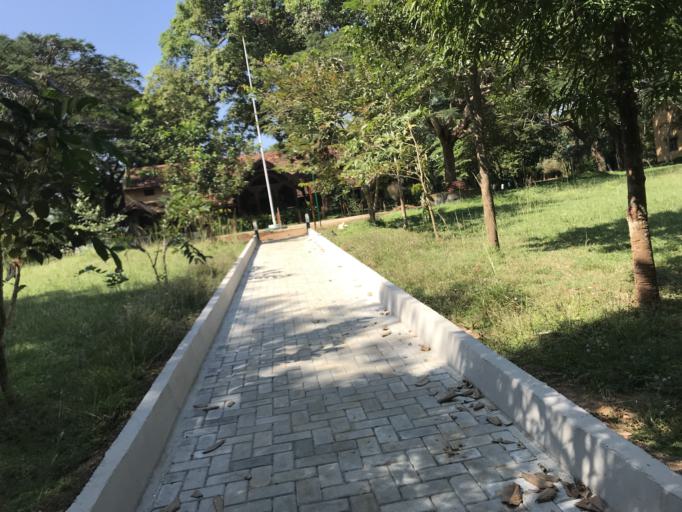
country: IN
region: Karnataka
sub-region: Mysore
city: Sargur
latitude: 11.9391
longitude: 76.2698
